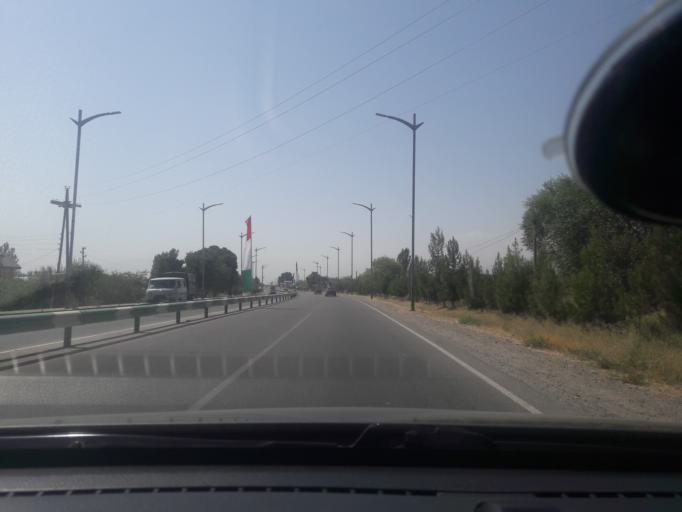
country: TJ
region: Republican Subordination
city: Hisor
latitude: 38.5610
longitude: 68.4465
